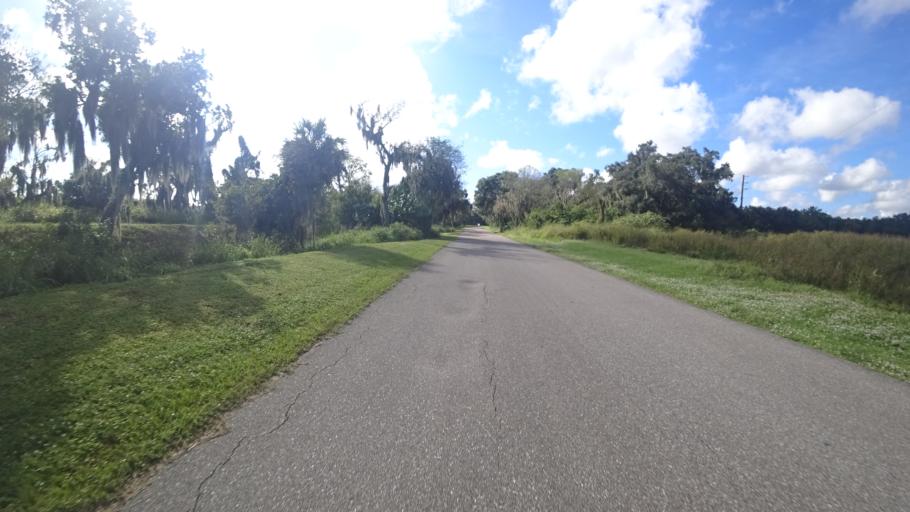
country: US
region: Florida
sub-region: Manatee County
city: Ellenton
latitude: 27.5762
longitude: -82.4748
